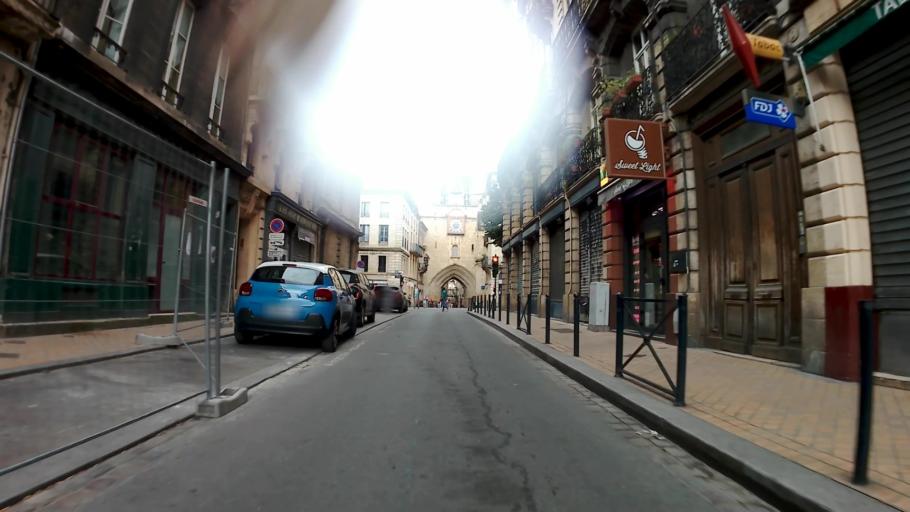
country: FR
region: Aquitaine
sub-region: Departement de la Gironde
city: Bordeaux
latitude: 44.8345
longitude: -0.5712
